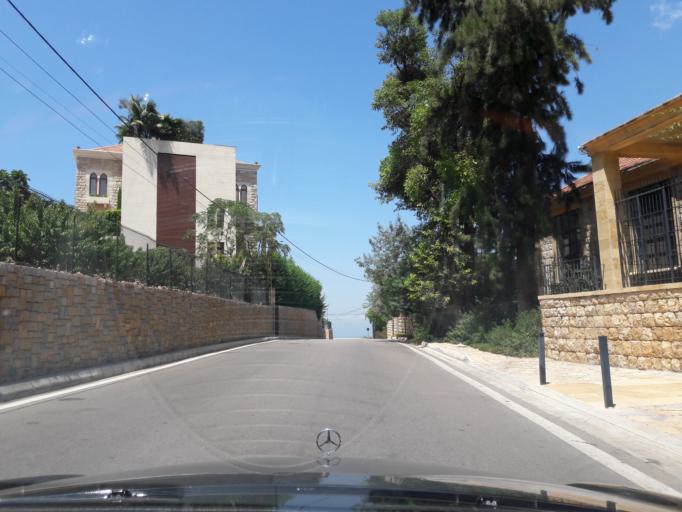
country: LB
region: Mont-Liban
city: Djounie
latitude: 33.9200
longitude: 35.6382
